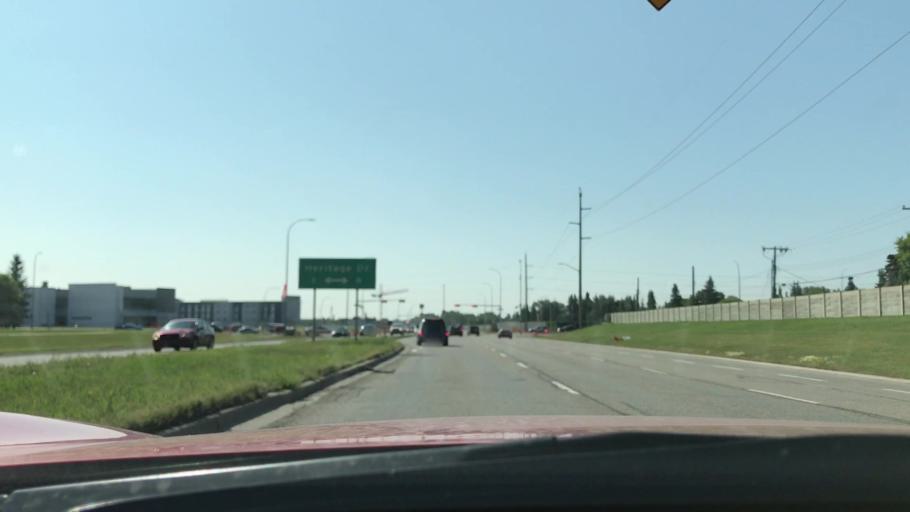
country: CA
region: Alberta
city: Calgary
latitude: 50.9823
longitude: -114.0513
